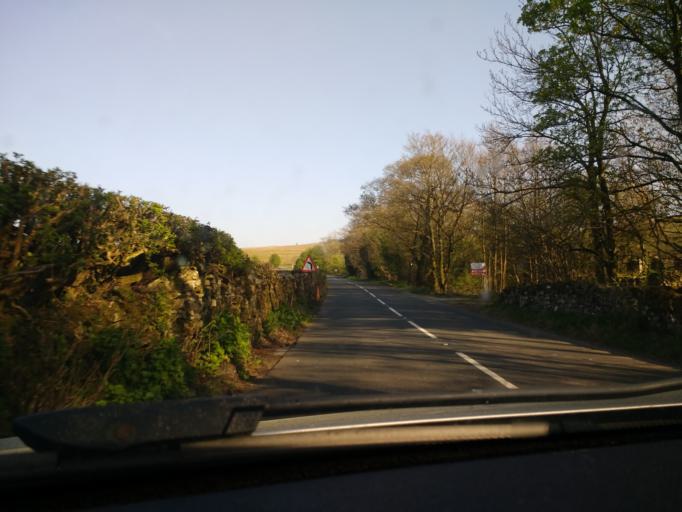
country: GB
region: England
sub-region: Cumbria
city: Sedbergh
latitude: 54.3174
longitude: -2.4863
